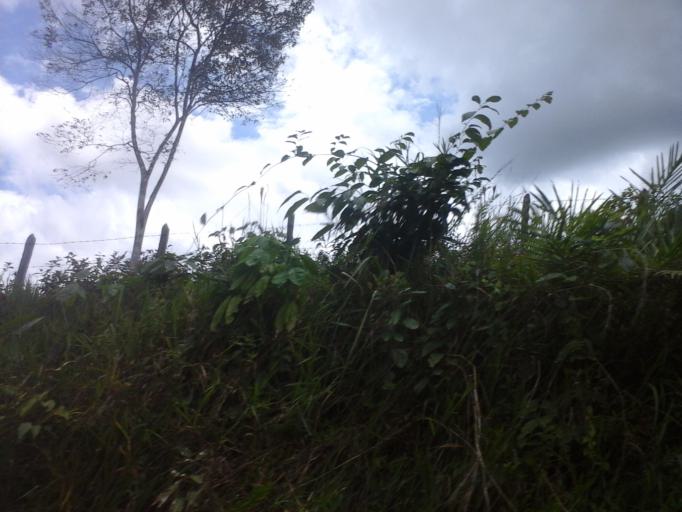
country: CO
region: Caqueta
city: El Doncello
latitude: 1.6423
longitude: -75.1683
